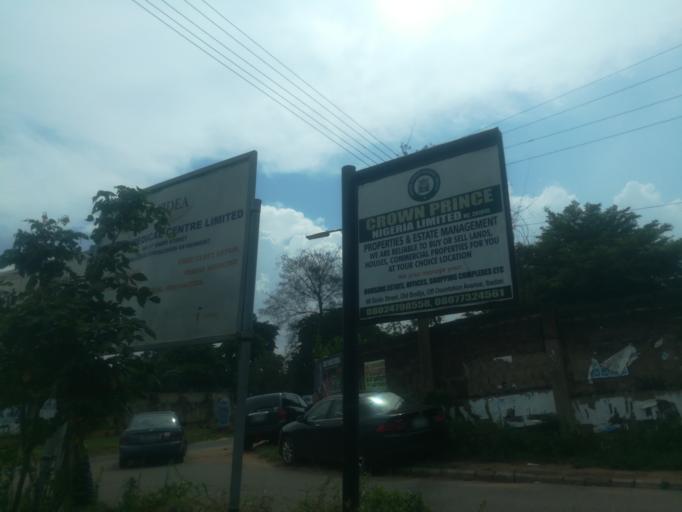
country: NG
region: Oyo
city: Ibadan
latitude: 7.4230
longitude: 3.9061
